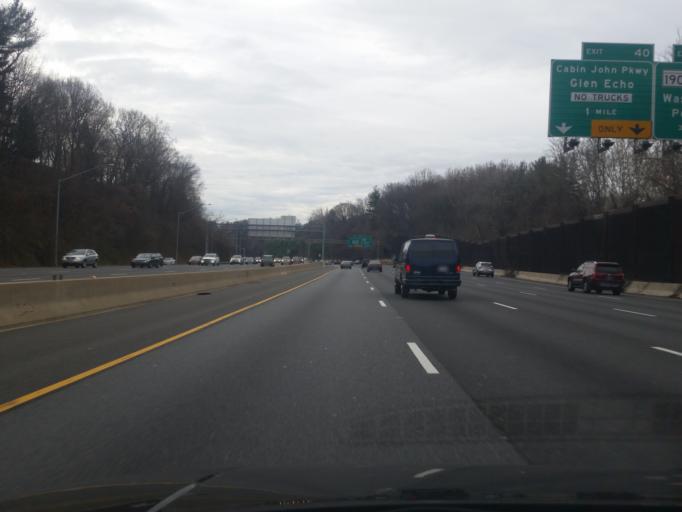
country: US
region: Maryland
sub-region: Montgomery County
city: Cabin John
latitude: 39.0031
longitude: -77.1554
